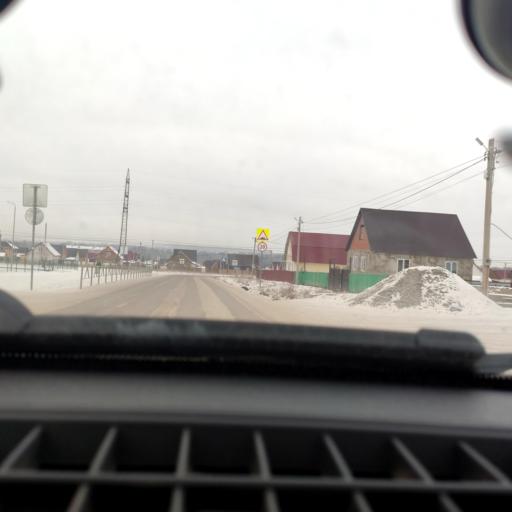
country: RU
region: Bashkortostan
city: Iglino
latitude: 54.8252
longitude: 56.4383
